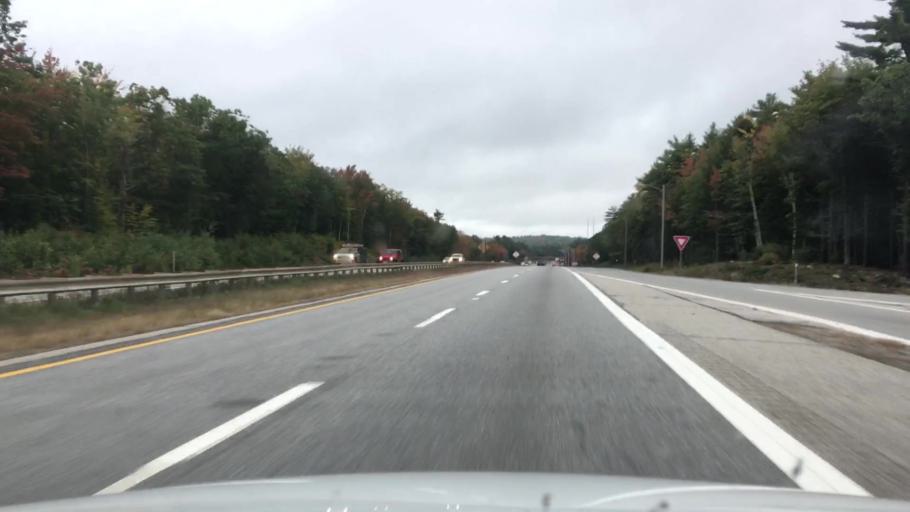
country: US
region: Maine
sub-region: Cumberland County
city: Cumberland Center
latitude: 43.8256
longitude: -70.3211
